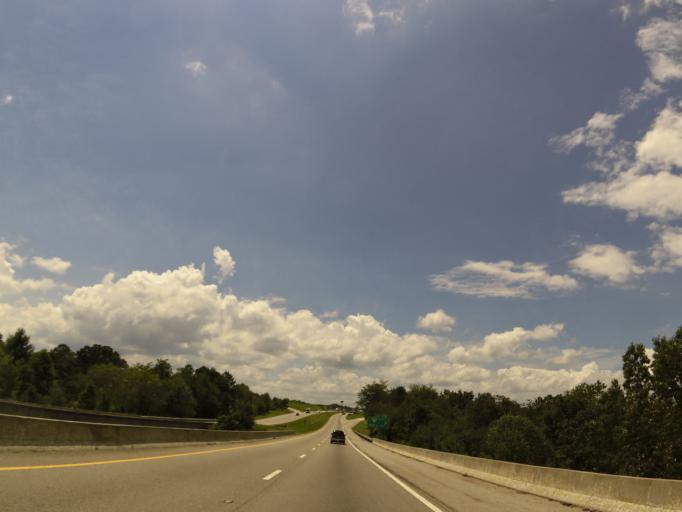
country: US
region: Tennessee
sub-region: Roane County
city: Rockwood
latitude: 35.8957
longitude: -84.7270
